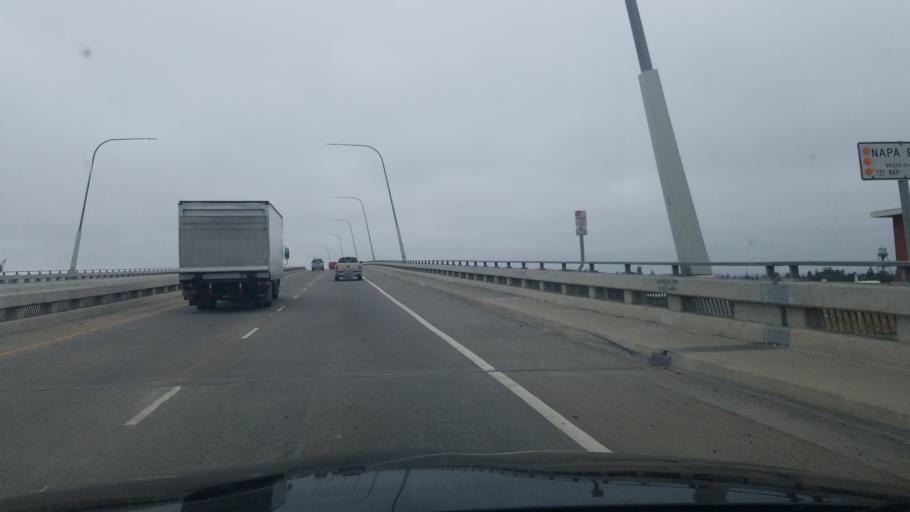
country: US
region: California
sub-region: Napa County
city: Napa
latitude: 38.2811
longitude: -122.2811
